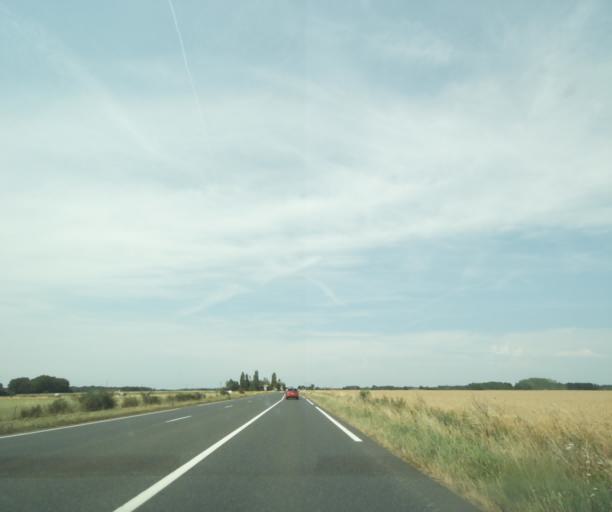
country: FR
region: Centre
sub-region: Departement d'Indre-et-Loire
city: Sorigny
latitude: 47.1960
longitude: 0.6682
